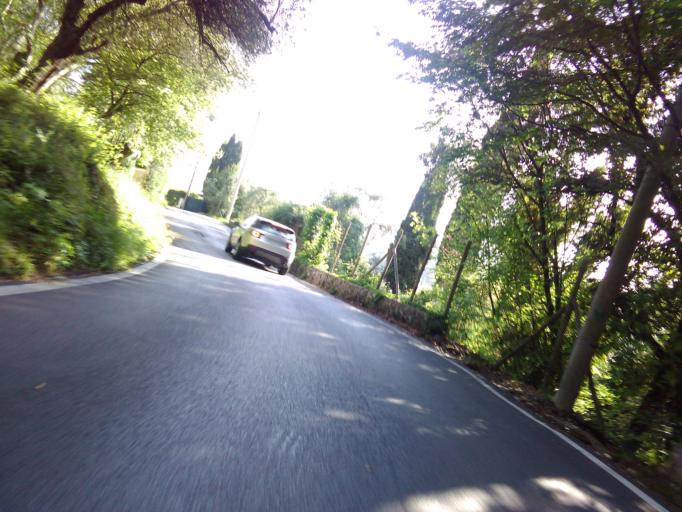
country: IT
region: Tuscany
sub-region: Provincia di Lucca
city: Piano di Mommio
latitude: 43.9440
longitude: 10.2626
